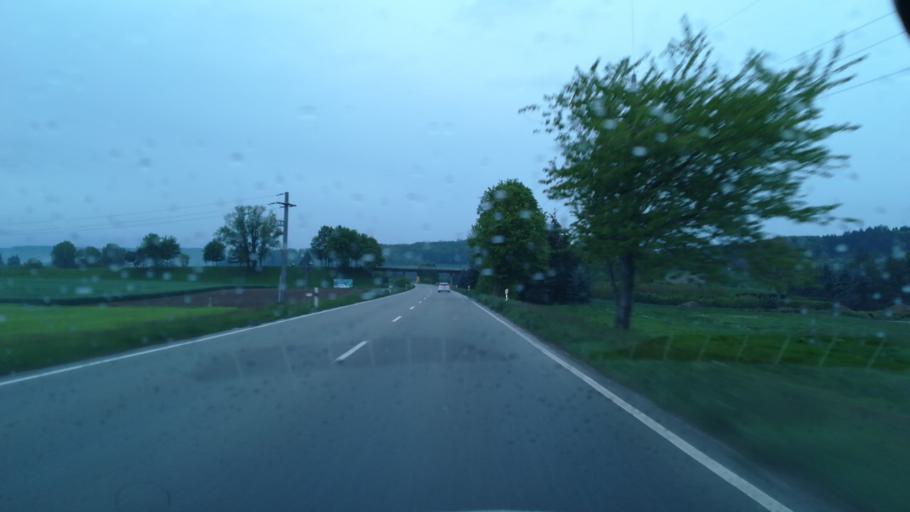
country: DE
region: Baden-Wuerttemberg
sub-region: Freiburg Region
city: Lottstetten
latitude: 47.6276
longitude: 8.5799
